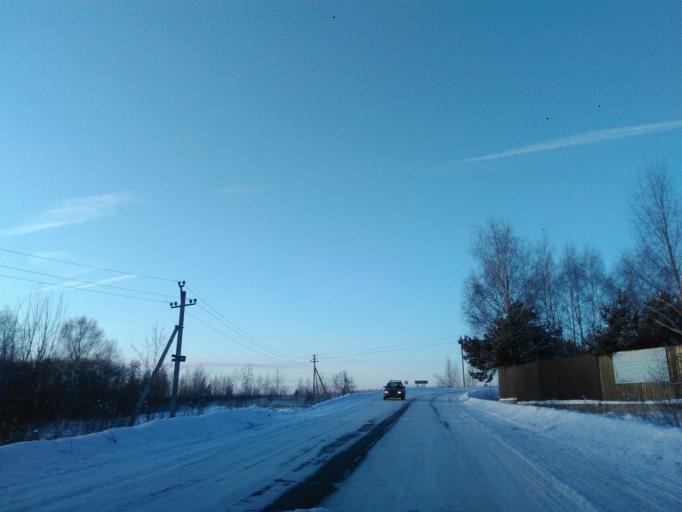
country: RU
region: Tverskaya
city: Zavidovo
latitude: 56.6082
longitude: 36.6127
